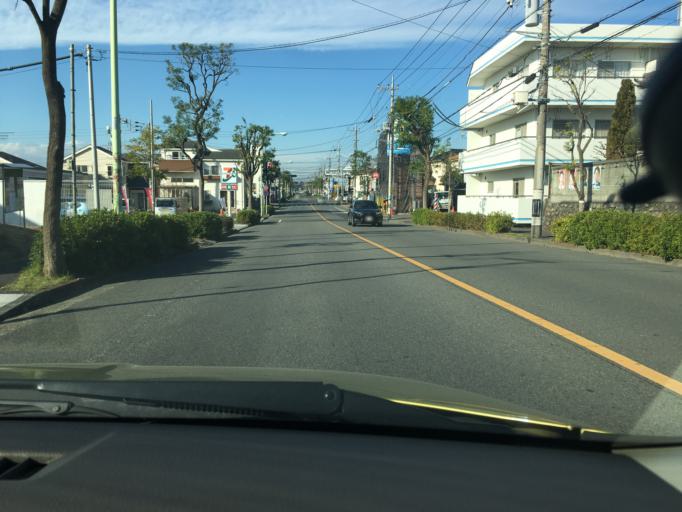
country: JP
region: Tokyo
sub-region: Machida-shi
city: Machida
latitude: 35.5663
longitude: 139.4189
